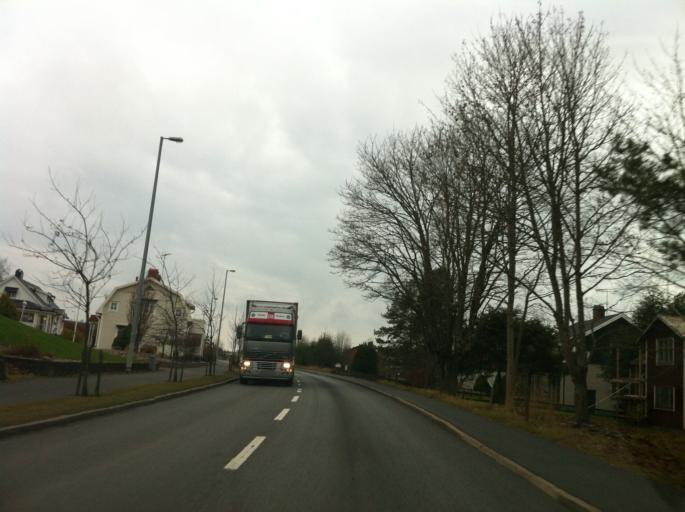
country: SE
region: Joenkoeping
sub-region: Savsjo Kommun
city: Stockaryd
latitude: 57.3756
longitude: 14.5466
